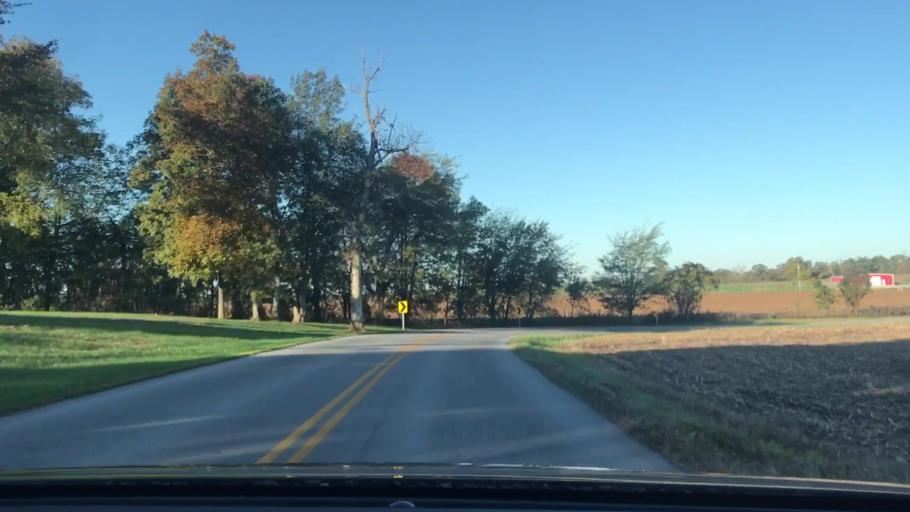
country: US
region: Kentucky
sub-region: Logan County
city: Auburn
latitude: 36.8284
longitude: -86.6795
